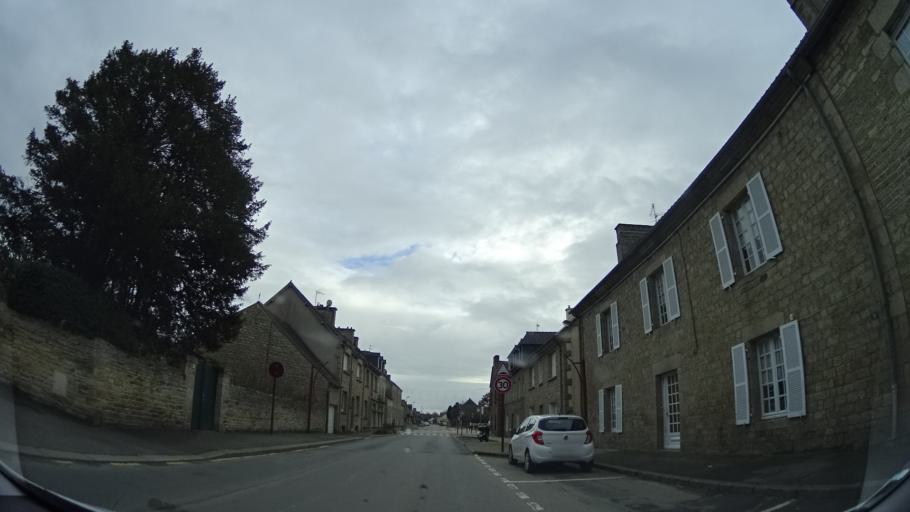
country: FR
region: Brittany
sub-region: Departement des Cotes-d'Armor
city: Evran
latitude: 48.3810
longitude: -1.9796
